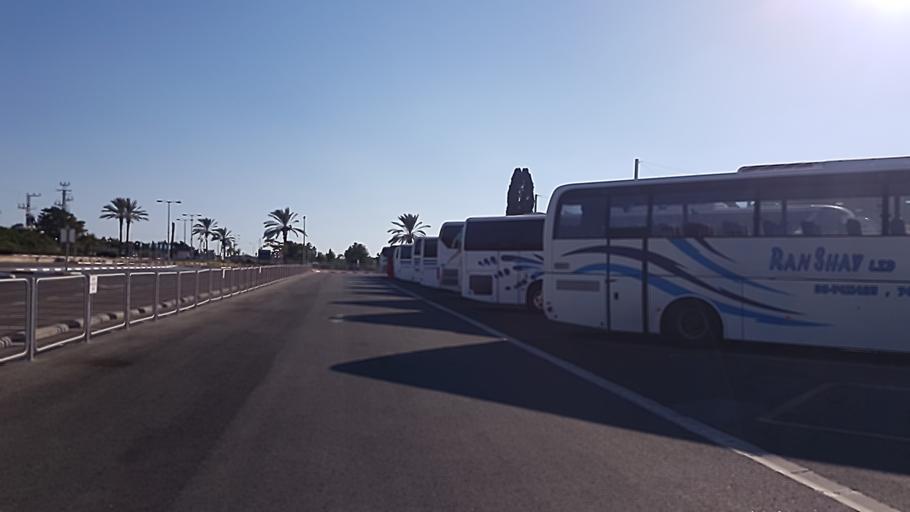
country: IL
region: Central District
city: Kfar Saba
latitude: 32.2012
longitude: 34.9232
